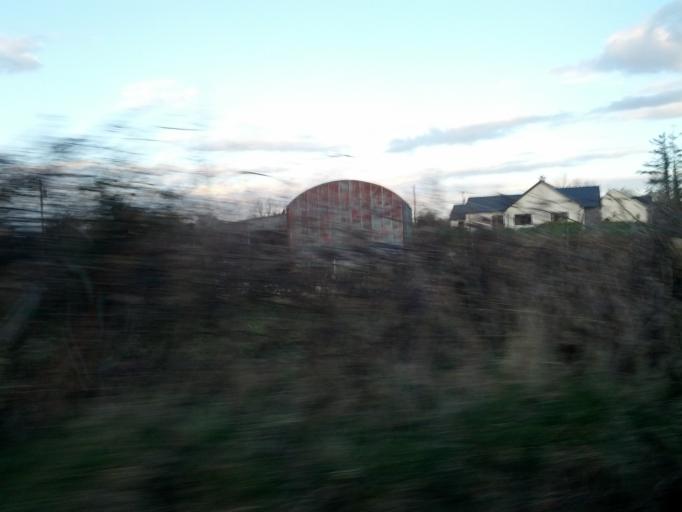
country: IE
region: Connaught
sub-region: County Galway
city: Athenry
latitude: 53.3237
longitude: -8.6210
